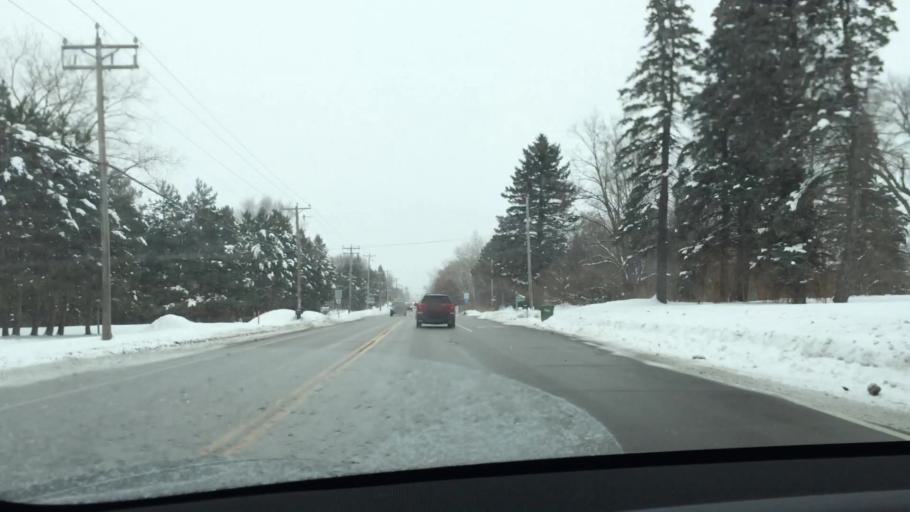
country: US
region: Minnesota
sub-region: Ramsey County
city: Shoreview
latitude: 45.1023
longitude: -93.1273
